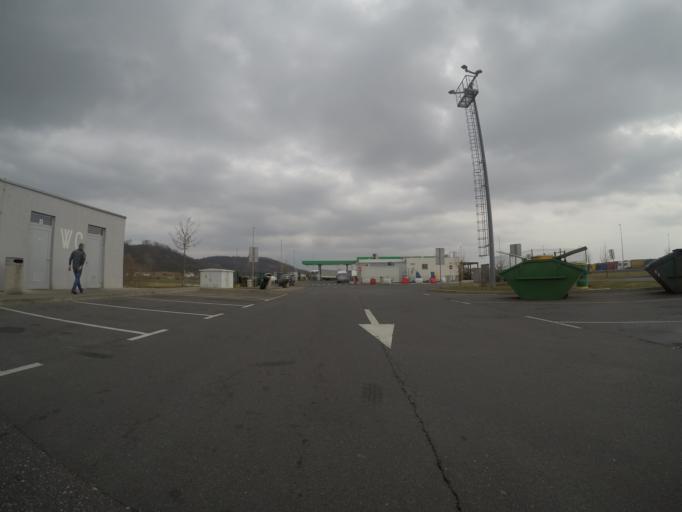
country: HR
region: Medimurska
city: Peklenica
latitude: 46.5228
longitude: 16.5186
